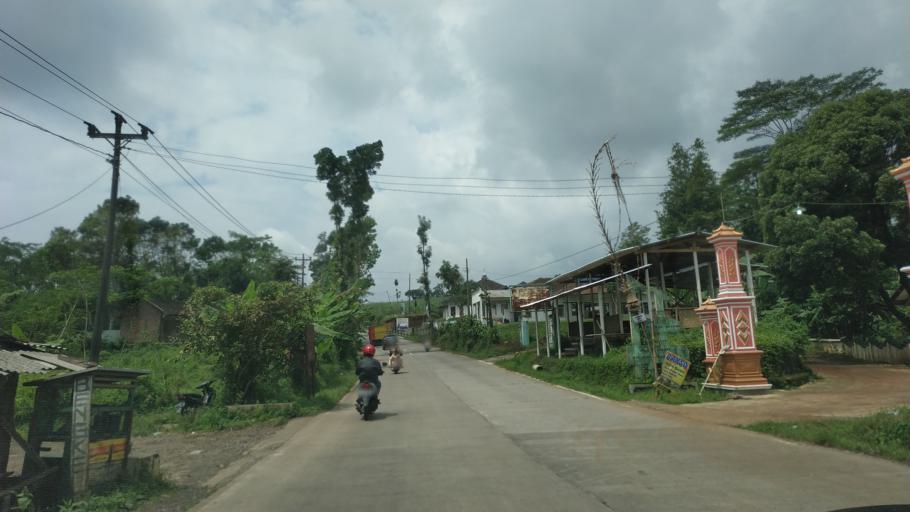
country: ID
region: Central Java
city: Weleri
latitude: -7.1004
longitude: 110.0655
